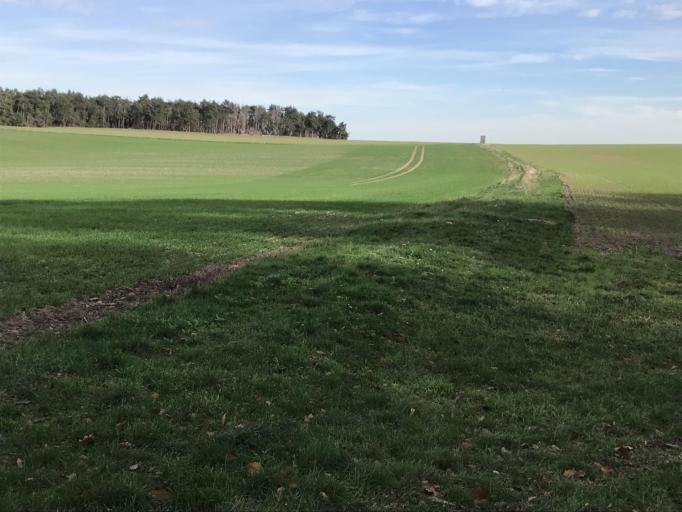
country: DE
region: Saxony-Anhalt
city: Derenburg
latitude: 51.8564
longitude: 10.9344
